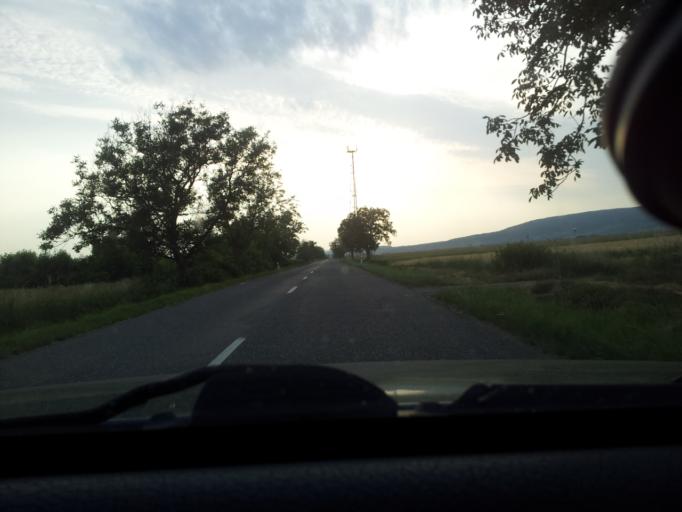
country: SK
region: Nitriansky
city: Levice
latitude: 48.2826
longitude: 18.6211
